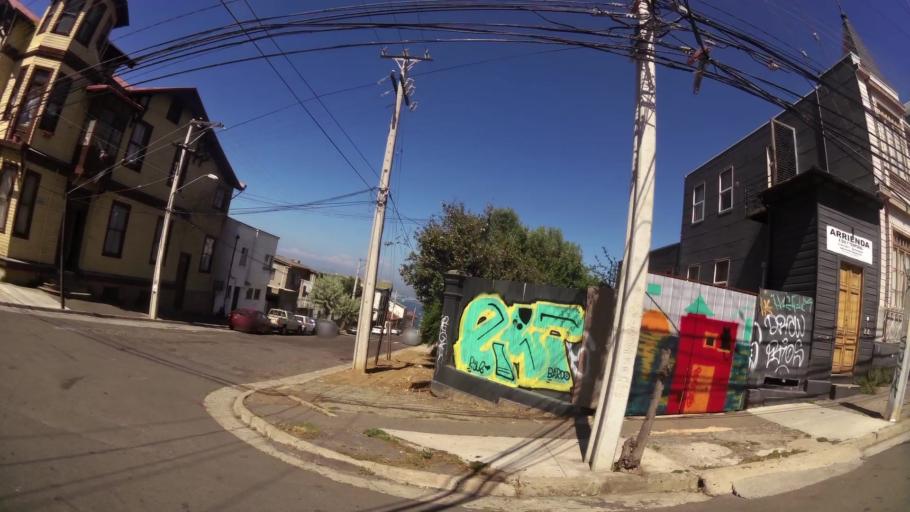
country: CL
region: Valparaiso
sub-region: Provincia de Valparaiso
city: Valparaiso
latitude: -33.0277
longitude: -71.6336
